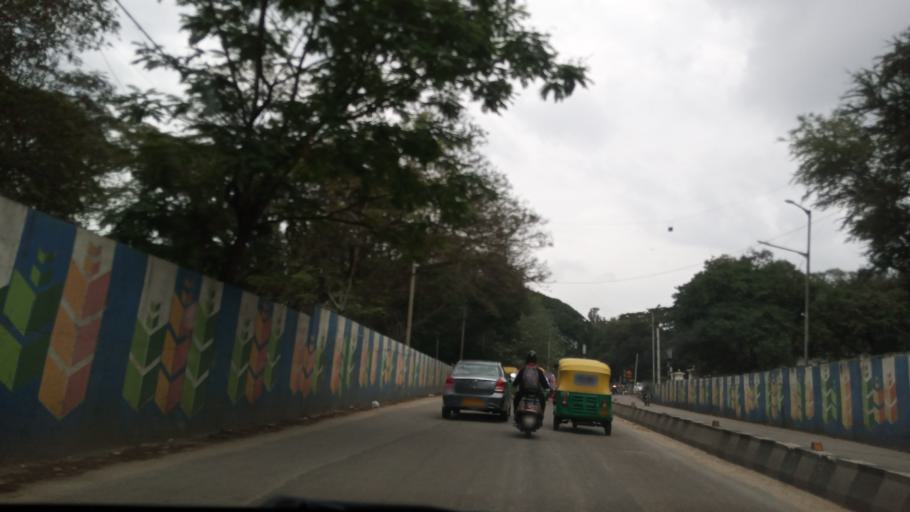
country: IN
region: Karnataka
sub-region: Bangalore Urban
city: Bangalore
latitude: 12.9953
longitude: 77.5960
